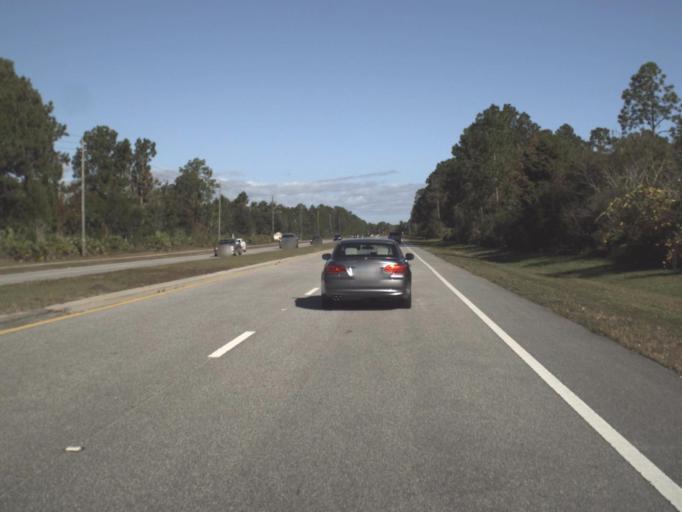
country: US
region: Florida
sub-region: Volusia County
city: Ormond Beach
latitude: 29.2515
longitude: -81.0937
